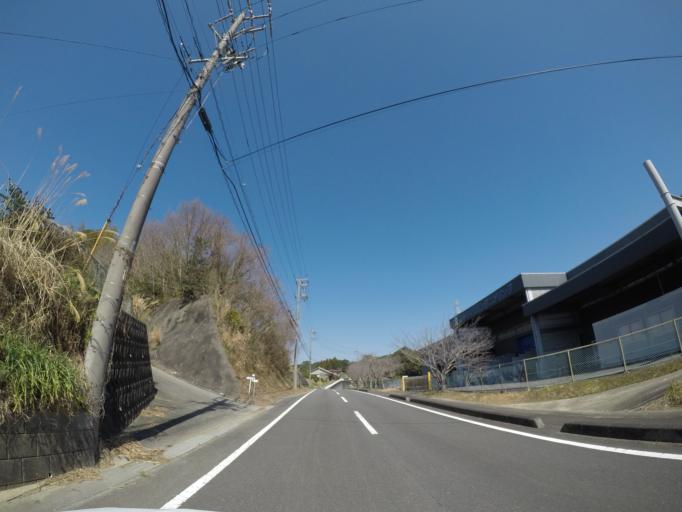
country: JP
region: Shizuoka
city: Kanaya
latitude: 34.7838
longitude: 138.1086
